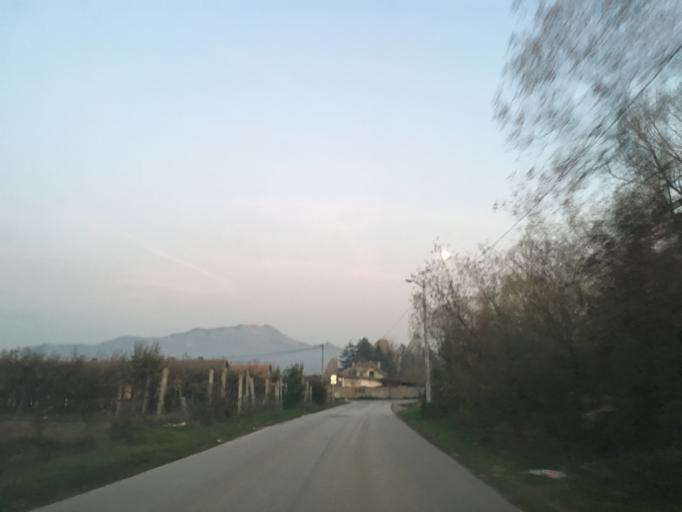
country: BA
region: Federation of Bosnia and Herzegovina
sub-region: Kanton Sarajevo
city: Sarajevo
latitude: 43.8164
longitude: 18.3455
